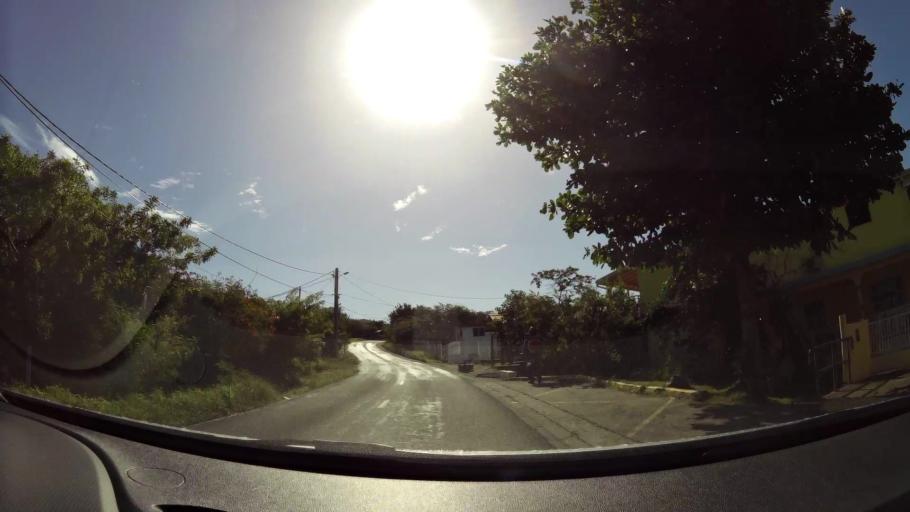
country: MQ
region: Martinique
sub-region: Martinique
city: Les Trois-Ilets
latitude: 14.4617
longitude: -61.0664
